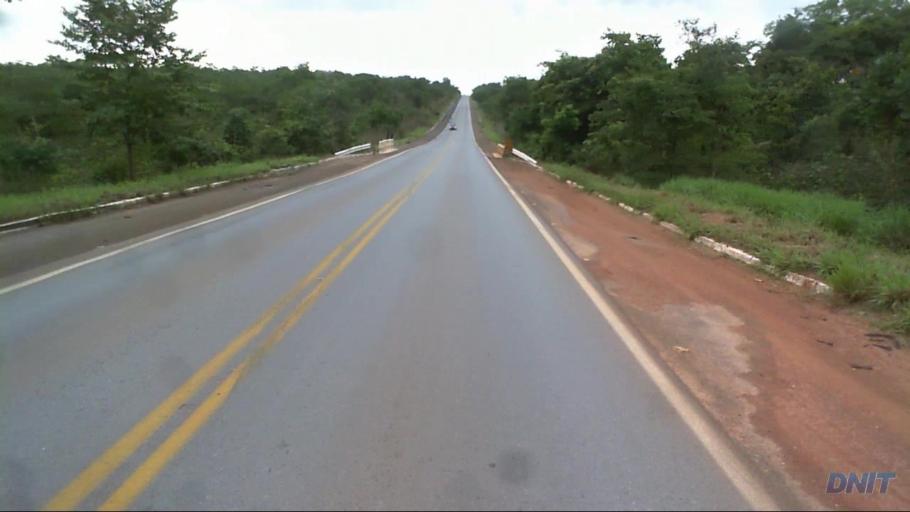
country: BR
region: Goias
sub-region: Uruacu
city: Uruacu
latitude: -14.7525
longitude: -49.0718
